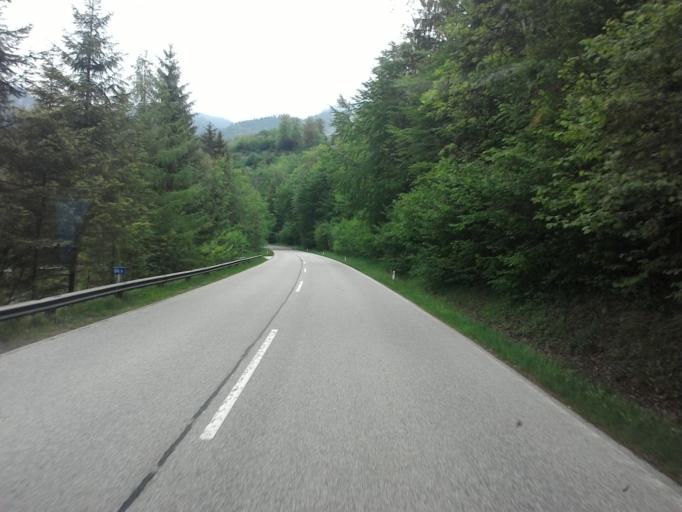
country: AT
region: Styria
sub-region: Politischer Bezirk Liezen
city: Altenmarkt bei Sankt Gallen
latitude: 47.7036
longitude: 14.6899
